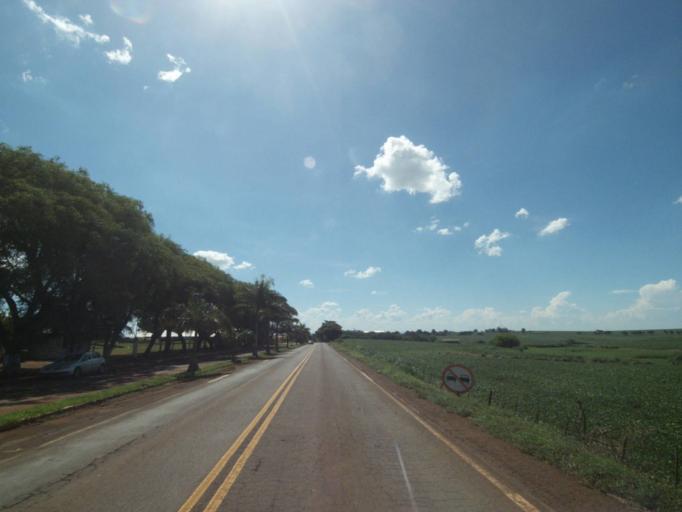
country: BR
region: Parana
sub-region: Sertanopolis
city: Sertanopolis
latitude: -23.0344
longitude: -50.8115
